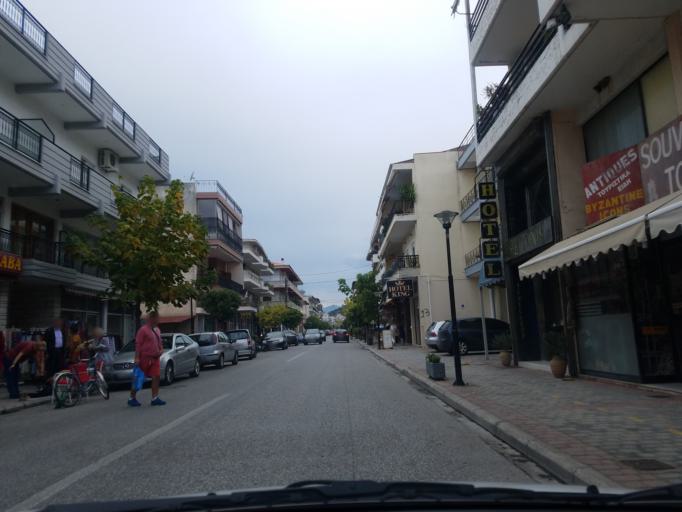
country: GR
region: Thessaly
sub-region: Trikala
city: Kalampaka
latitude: 39.7031
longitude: 21.6311
